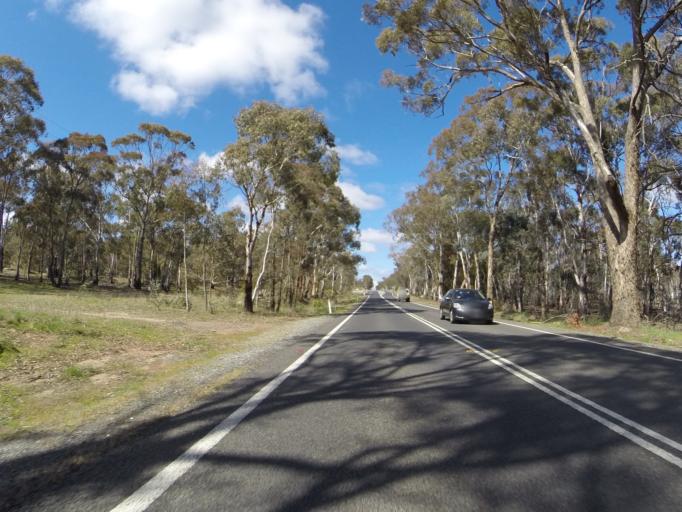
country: AU
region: New South Wales
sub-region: Queanbeyan
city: Queanbeyan
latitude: -35.2529
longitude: 149.2623
